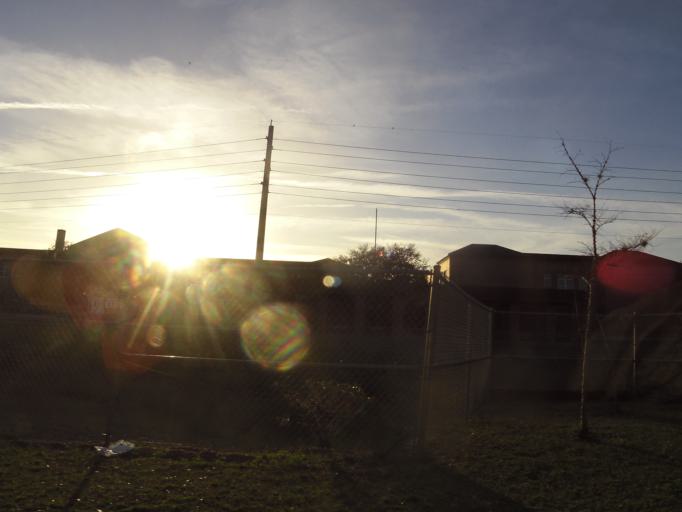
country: US
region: Florida
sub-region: Duval County
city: Jacksonville
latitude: 30.3415
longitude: -81.6389
